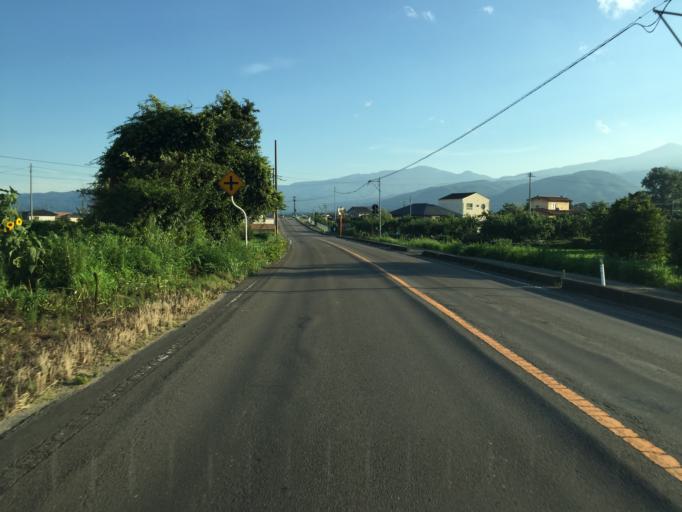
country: JP
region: Fukushima
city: Fukushima-shi
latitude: 37.7749
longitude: 140.3869
